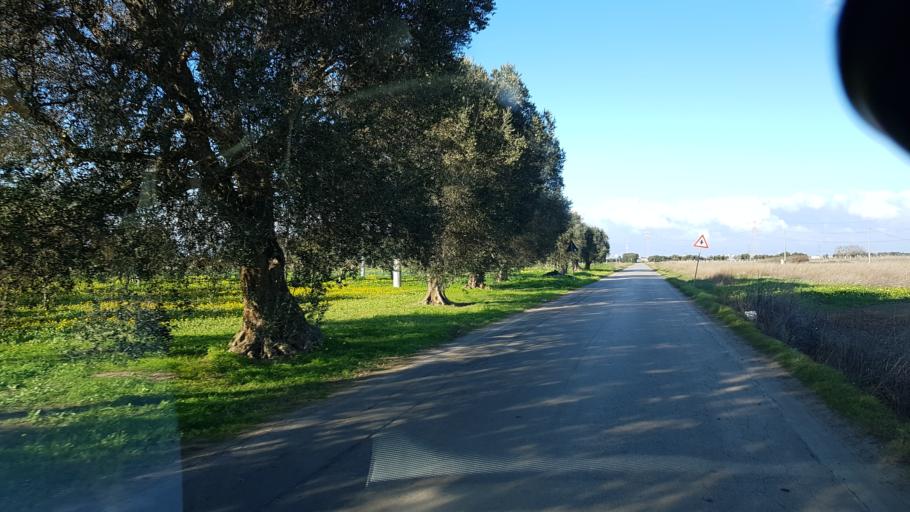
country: IT
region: Apulia
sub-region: Provincia di Brindisi
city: La Rosa
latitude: 40.5793
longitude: 17.9019
